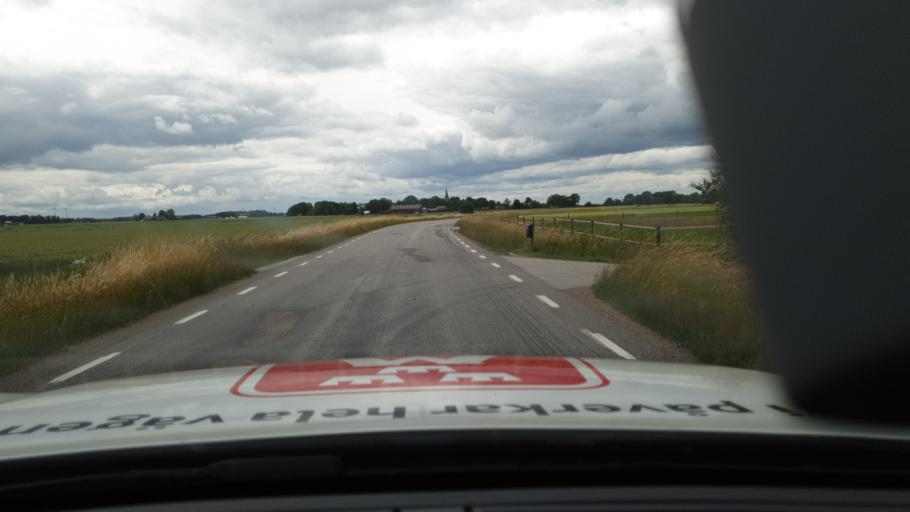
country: SE
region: Vaestra Goetaland
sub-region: Lidkopings Kommun
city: Vinninga
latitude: 58.3827
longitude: 13.2978
